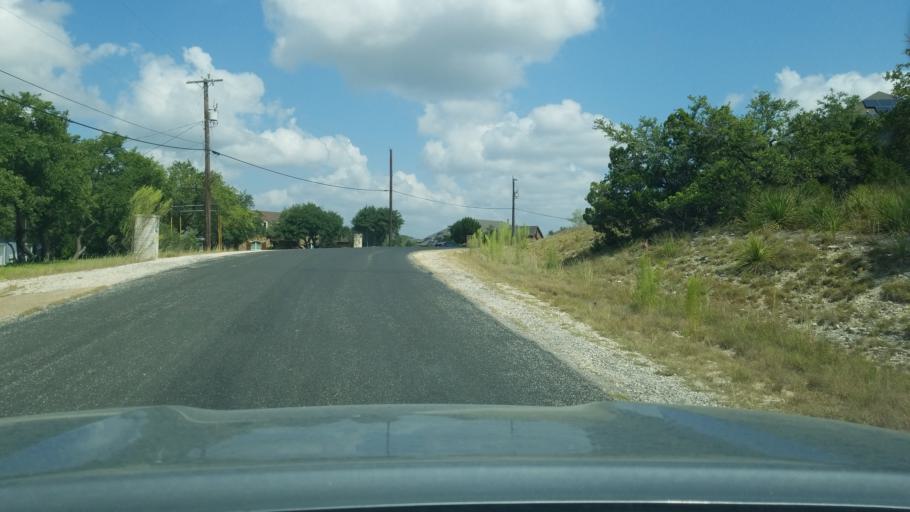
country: US
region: Texas
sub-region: Bexar County
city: Timberwood Park
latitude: 29.6767
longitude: -98.5212
